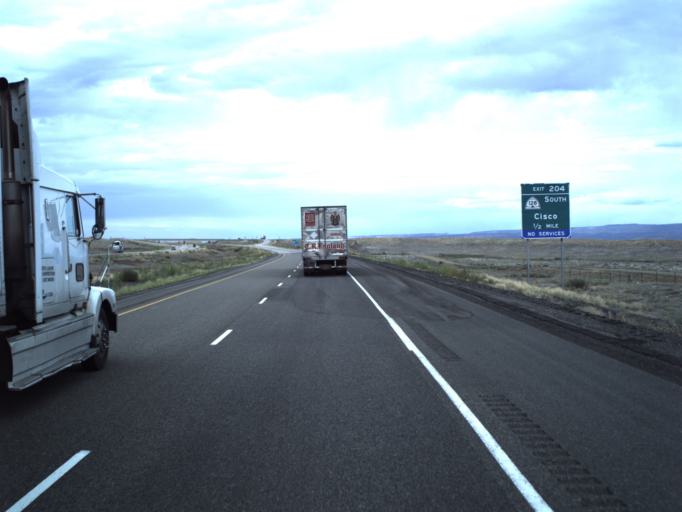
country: US
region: Utah
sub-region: Grand County
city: Moab
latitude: 38.9337
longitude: -109.4198
